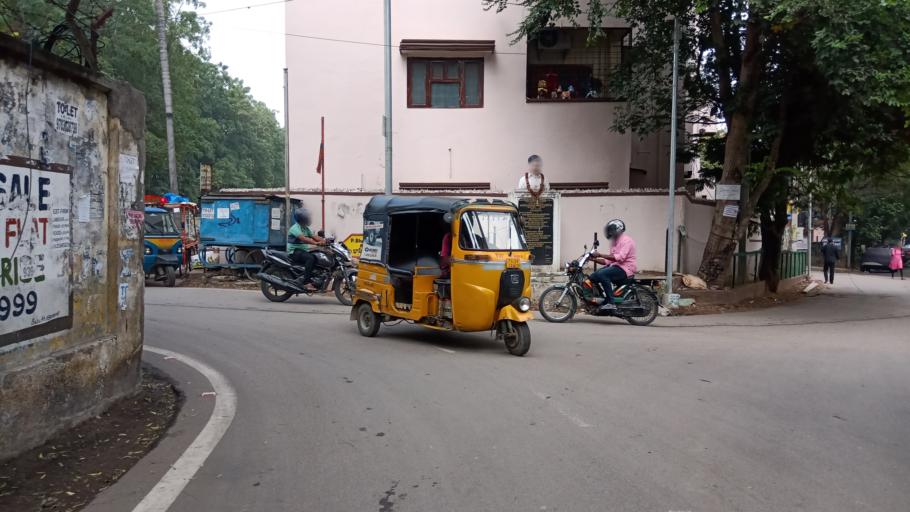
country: IN
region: Telangana
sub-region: Rangareddi
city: Kukatpalli
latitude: 17.4475
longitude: 78.4418
